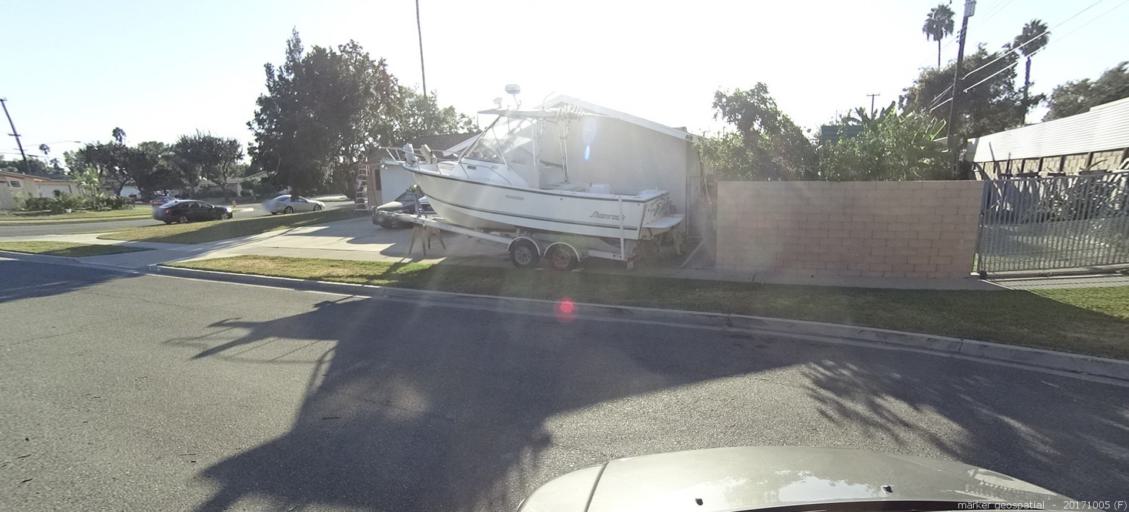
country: US
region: California
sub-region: Orange County
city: Stanton
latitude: 33.7983
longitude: -117.9821
